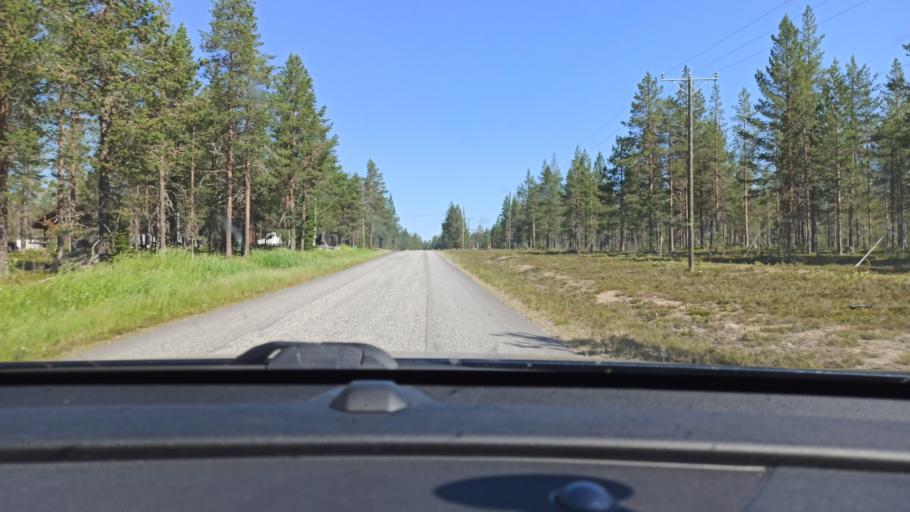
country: FI
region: Lapland
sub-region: Tunturi-Lappi
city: Kolari
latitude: 67.6533
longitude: 24.1631
